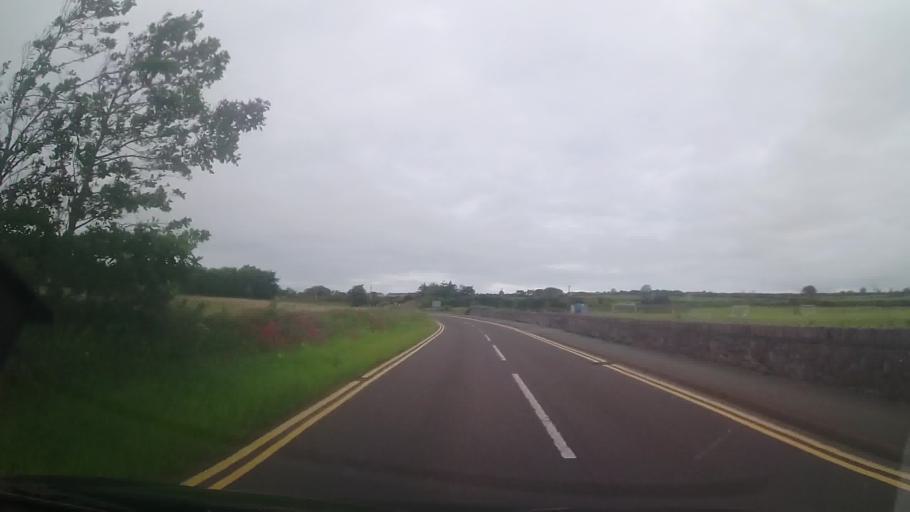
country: GB
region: Wales
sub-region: Gwynedd
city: Caernarfon
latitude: 53.1600
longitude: -4.3510
